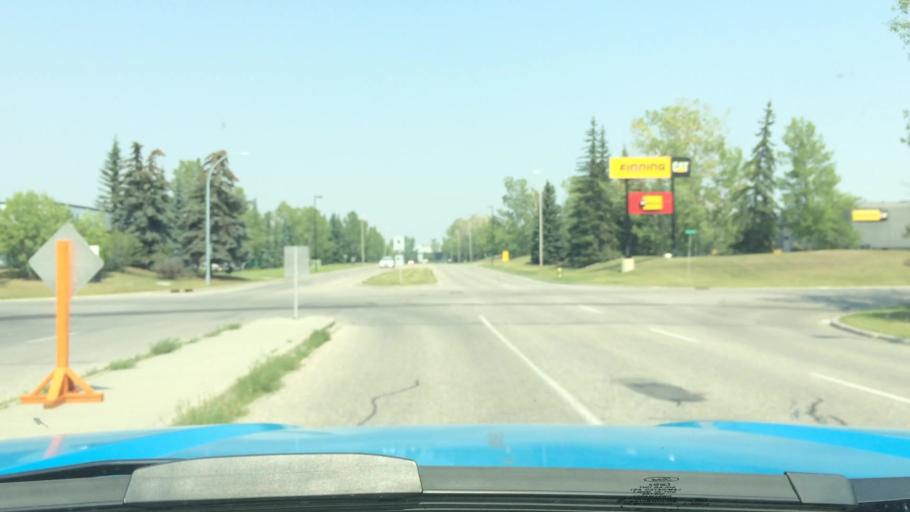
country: CA
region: Alberta
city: Calgary
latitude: 51.1119
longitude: -114.0413
